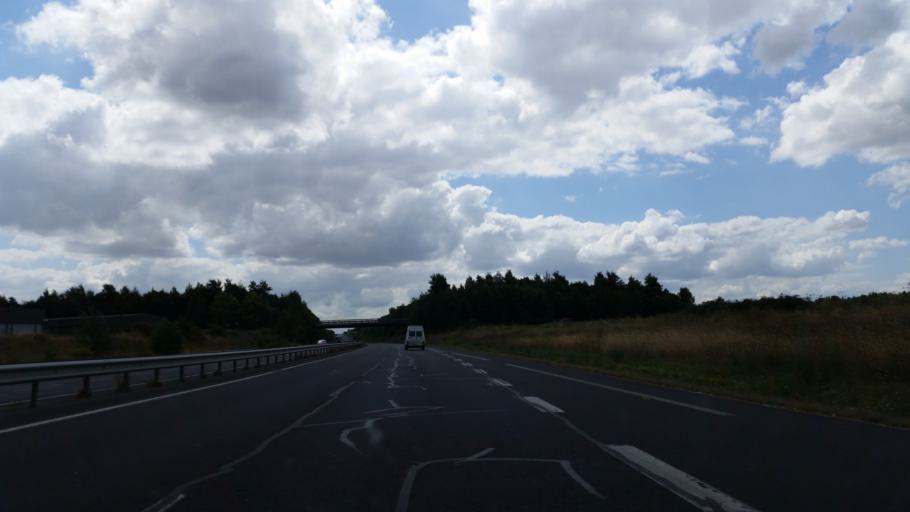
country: FR
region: Lower Normandy
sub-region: Departement du Calvados
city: Falaise
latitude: 48.9093
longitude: -0.2119
